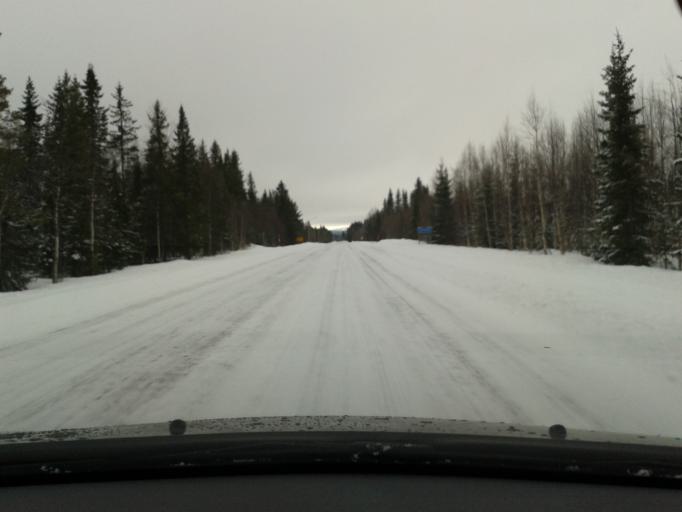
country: SE
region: Vaesterbotten
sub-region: Vilhelmina Kommun
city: Sjoberg
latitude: 64.8438
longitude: 15.9157
